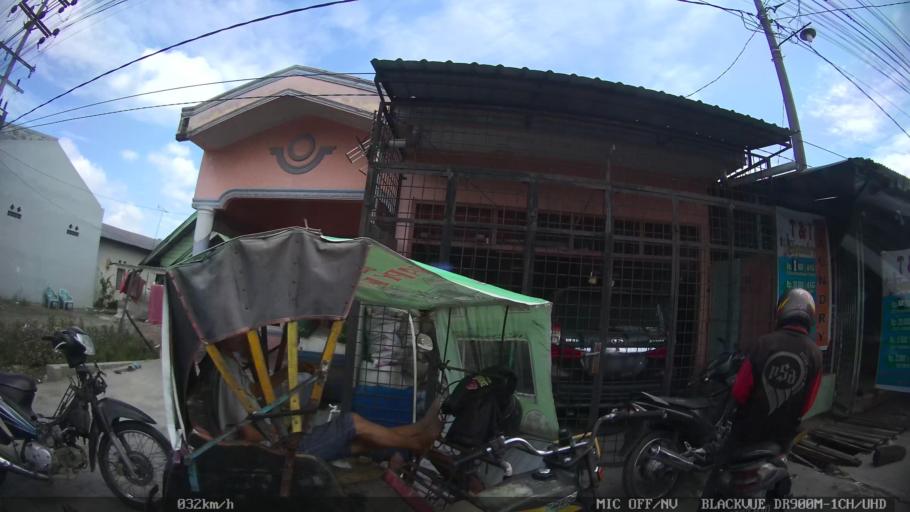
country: ID
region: North Sumatra
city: Medan
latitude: 3.6021
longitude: 98.7650
